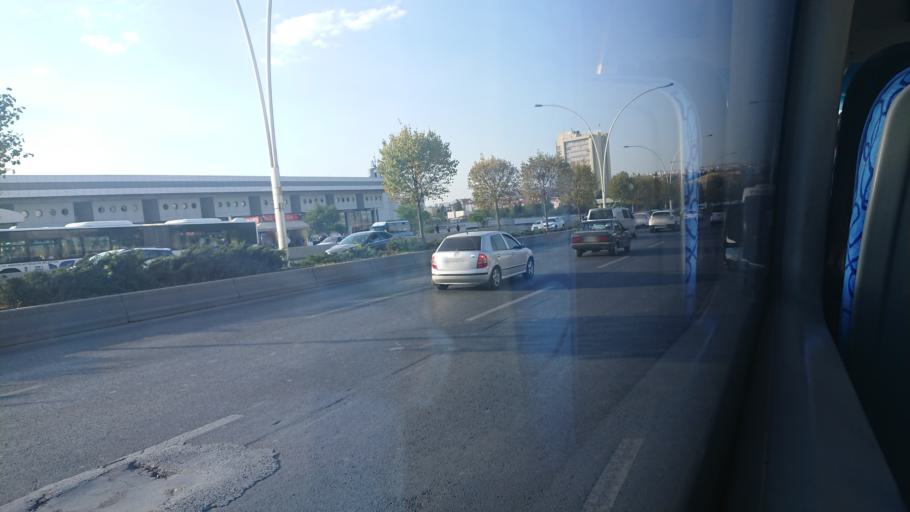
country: TR
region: Ankara
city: Ankara
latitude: 39.9177
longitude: 32.8142
